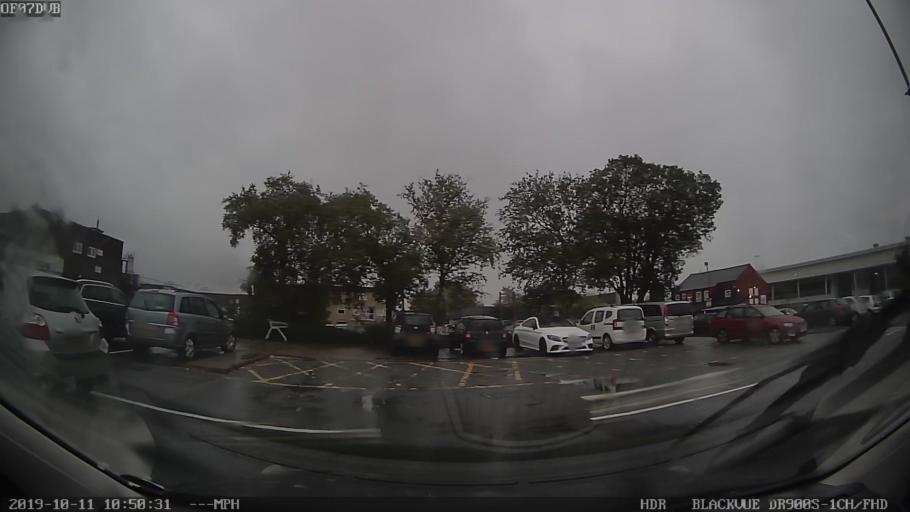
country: GB
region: England
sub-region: Borough of Oldham
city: Oldham
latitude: 53.5476
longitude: -2.1408
